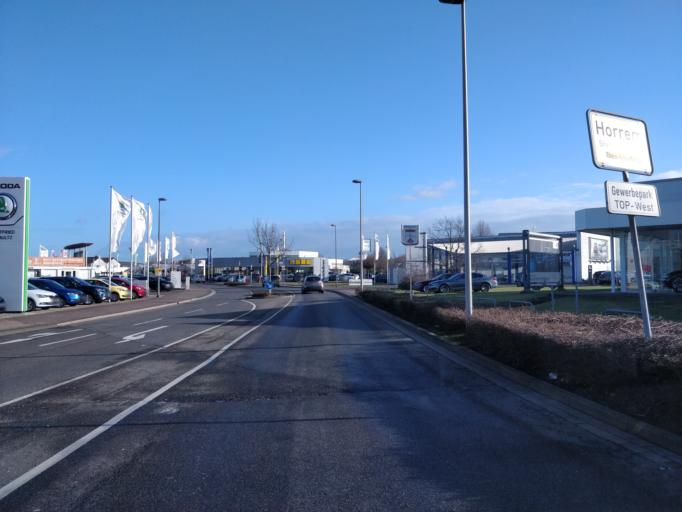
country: DE
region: North Rhine-Westphalia
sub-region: Regierungsbezirk Dusseldorf
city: Dormagen
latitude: 51.0908
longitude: 6.8122
